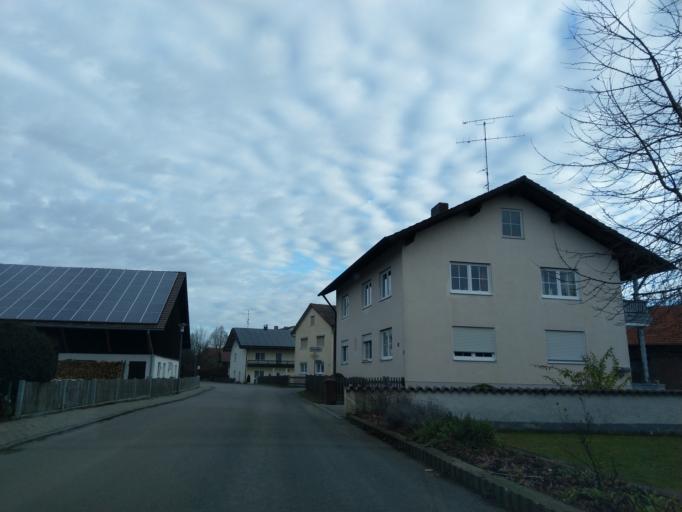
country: DE
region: Bavaria
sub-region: Lower Bavaria
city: Oberporing
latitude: 48.7031
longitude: 12.8273
